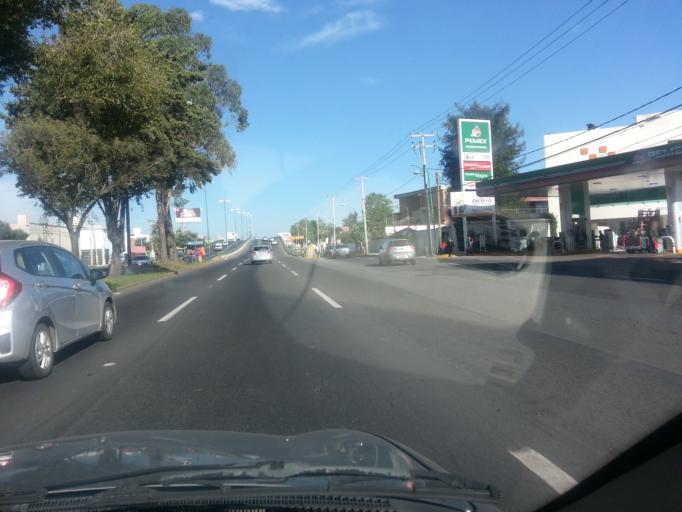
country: MX
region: Mexico
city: San Buenaventura
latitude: 19.2738
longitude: -99.6658
